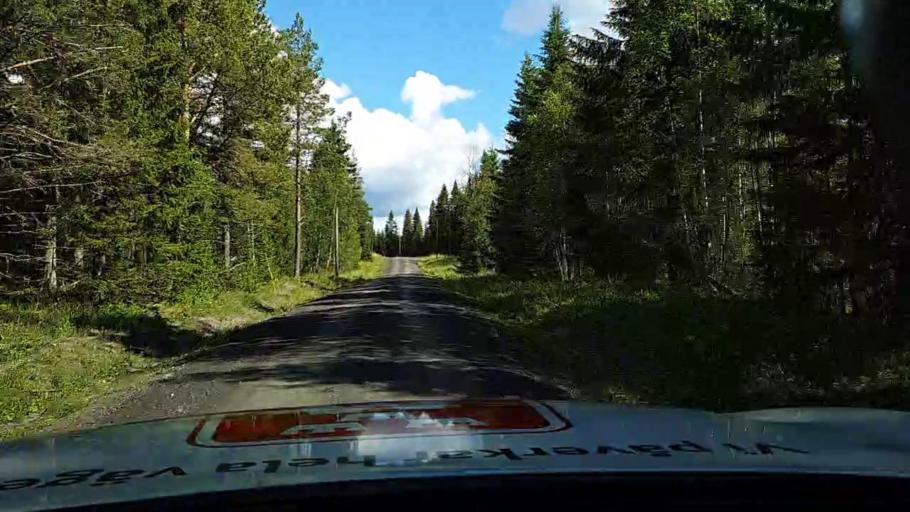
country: SE
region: Jaemtland
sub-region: Krokoms Kommun
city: Valla
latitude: 63.3332
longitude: 13.7218
